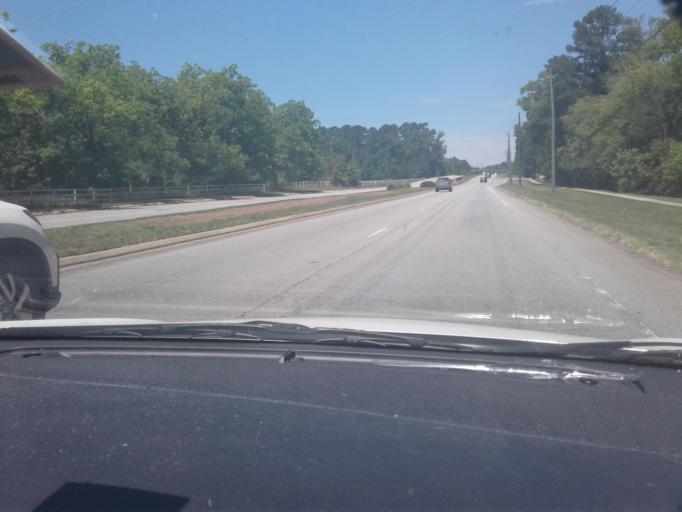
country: US
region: North Carolina
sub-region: Wake County
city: Holly Springs
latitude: 35.6286
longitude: -78.8234
